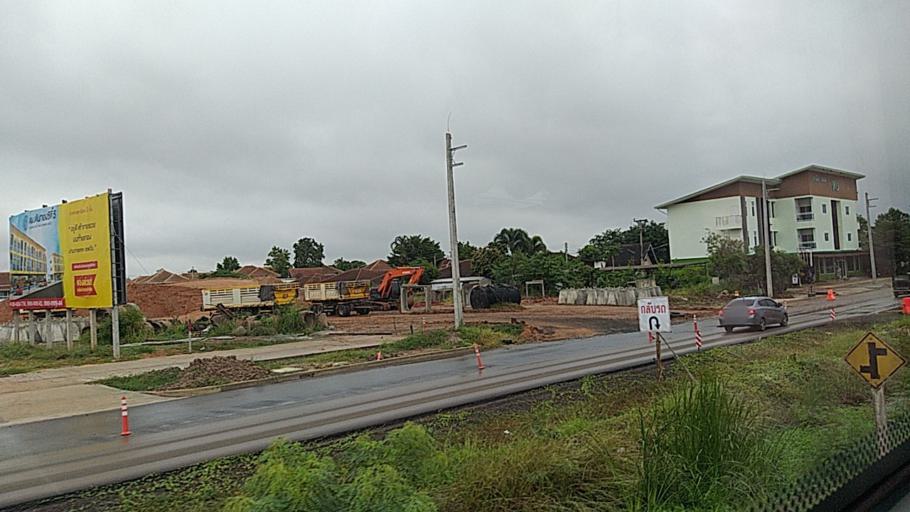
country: TH
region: Nakhon Ratchasima
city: Nakhon Ratchasima
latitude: 14.9951
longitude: 102.0672
